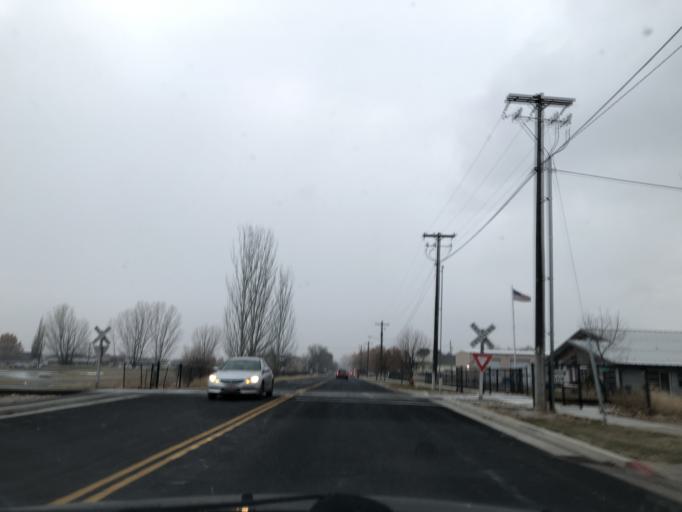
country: US
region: Utah
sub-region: Cache County
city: Logan
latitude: 41.7132
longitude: -111.8500
